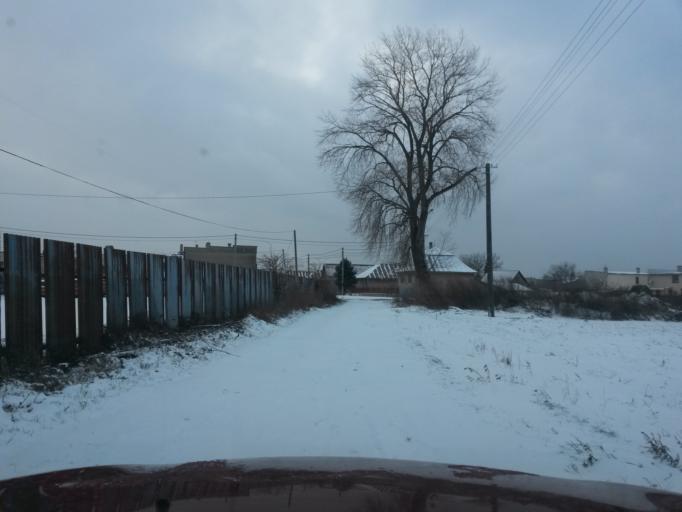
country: SK
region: Kosicky
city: Kosice
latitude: 48.6298
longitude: 21.3120
